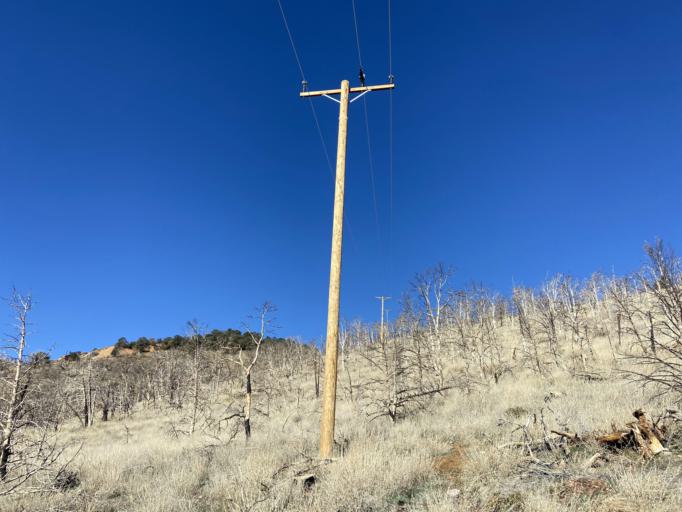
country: US
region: California
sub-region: San Bernardino County
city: Big Bear City
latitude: 34.3044
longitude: -116.8253
